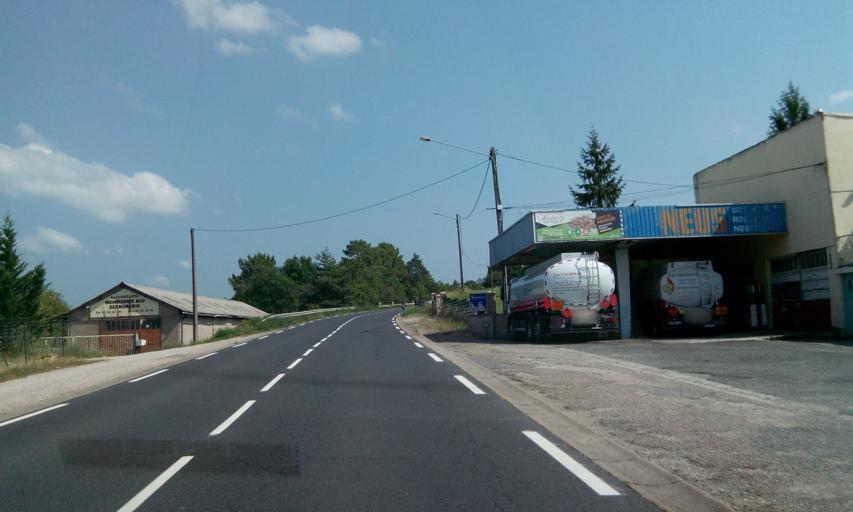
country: FR
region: Limousin
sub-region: Departement de la Correze
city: Cosnac
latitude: 45.1161
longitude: 1.5603
